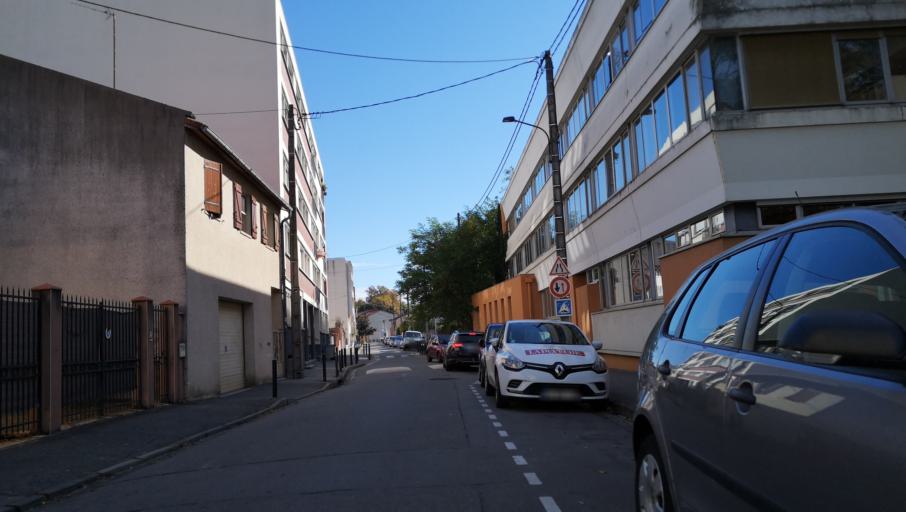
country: FR
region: Midi-Pyrenees
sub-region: Departement de la Haute-Garonne
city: Toulouse
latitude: 43.6073
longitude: 1.4186
